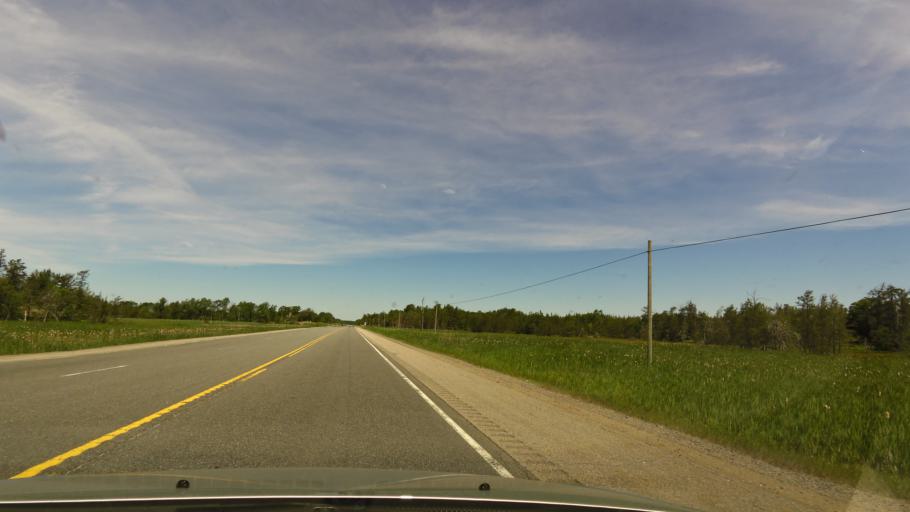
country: CA
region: Ontario
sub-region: Parry Sound District
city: Parry Sound
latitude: 45.4624
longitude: -80.1589
